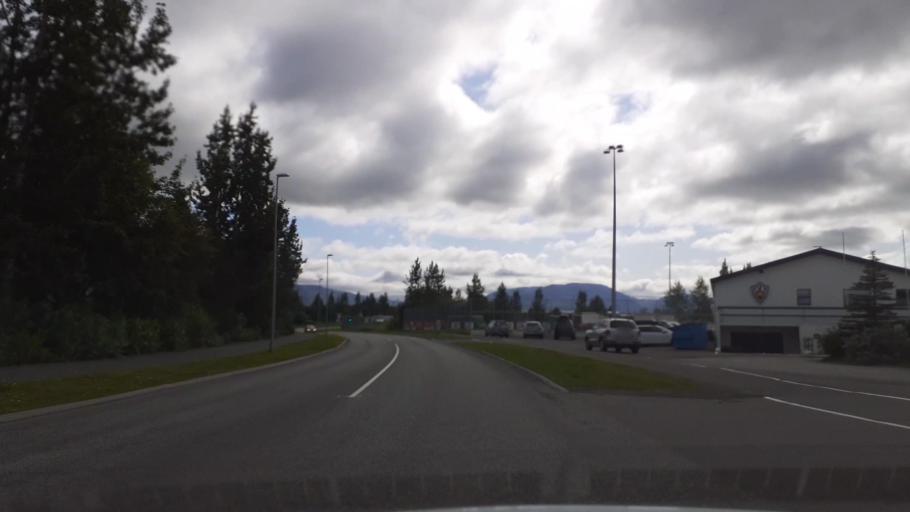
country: IS
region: Northeast
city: Akureyri
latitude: 65.6777
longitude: -18.1140
